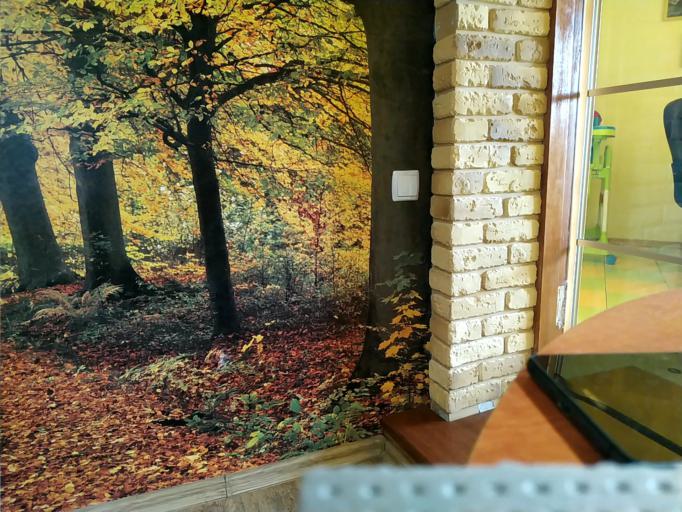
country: RU
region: Tverskaya
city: Zubtsov
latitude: 56.2268
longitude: 34.5242
